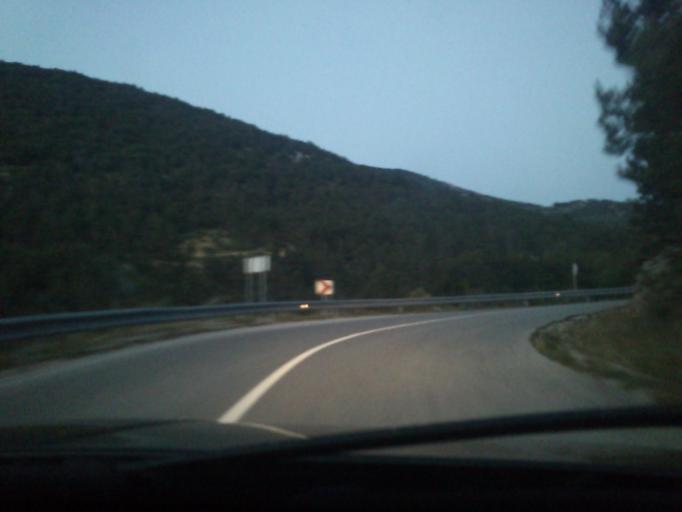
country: HR
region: Licko-Senjska
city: Senj
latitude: 44.8829
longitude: 14.9723
